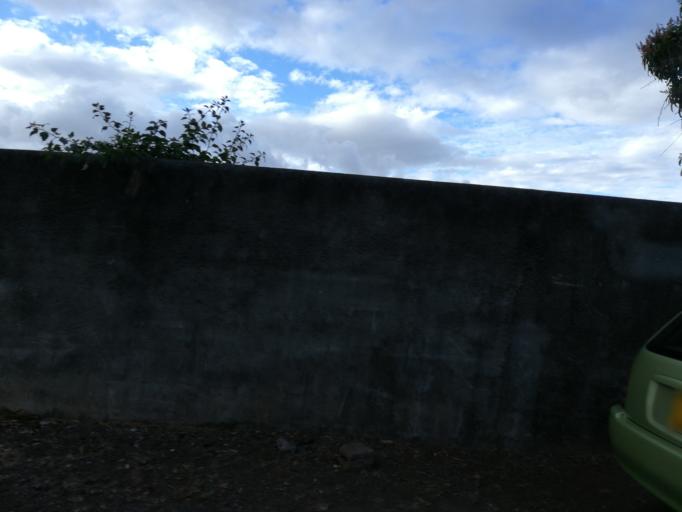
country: MU
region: Plaines Wilhems
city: Ebene
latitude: -20.2342
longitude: 57.4571
